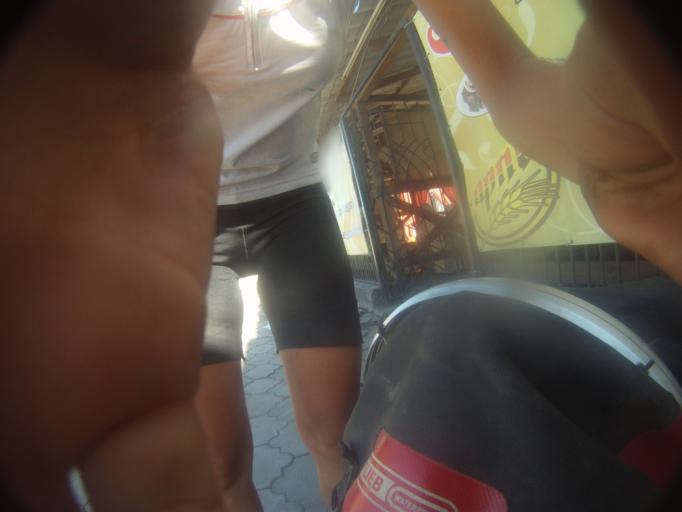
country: KG
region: Chuy
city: Bishkek
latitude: 42.8739
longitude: 74.4717
